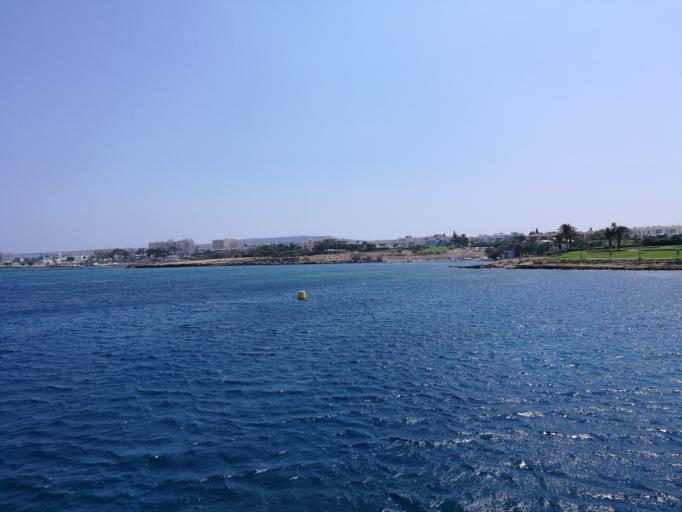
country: CY
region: Ammochostos
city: Protaras
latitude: 35.0442
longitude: 34.0358
